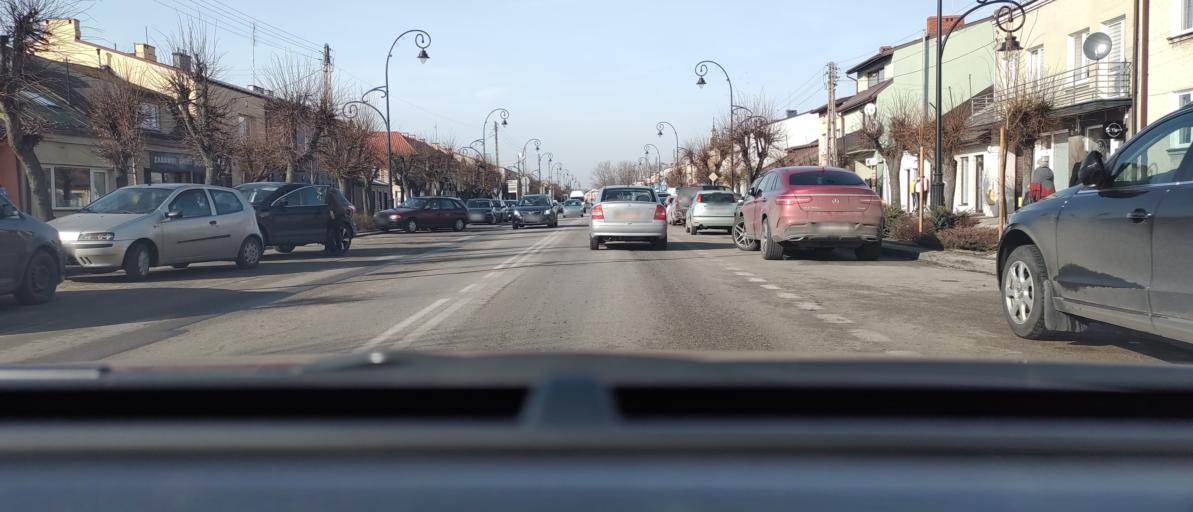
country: PL
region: Masovian Voivodeship
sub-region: Powiat bialobrzeski
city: Bialobrzegi
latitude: 51.6475
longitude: 20.9558
